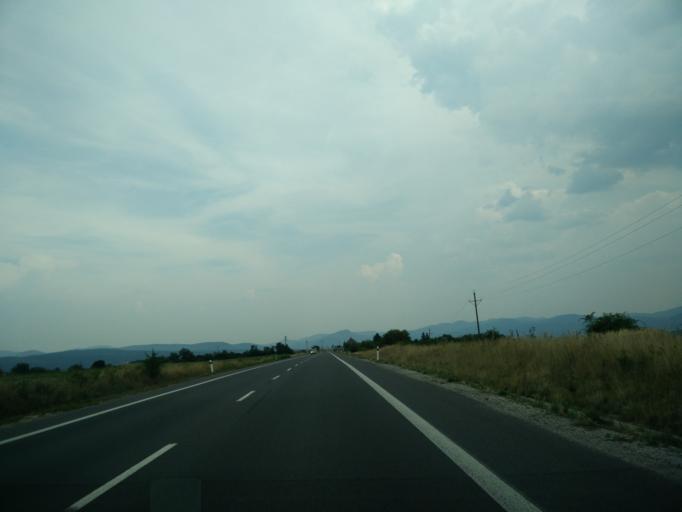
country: SK
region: Banskobystricky
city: Ziar nad Hronom
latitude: 48.6250
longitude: 18.7900
